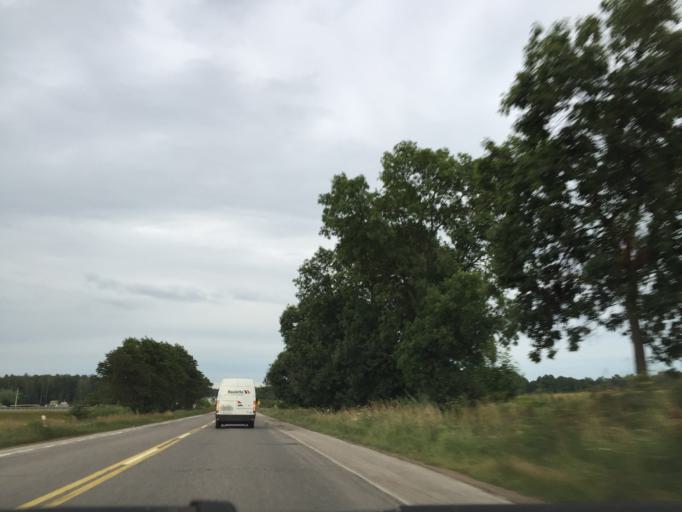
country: PL
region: Podlasie
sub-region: Powiat wysokomazowiecki
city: Sokoly
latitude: 53.1227
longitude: 22.6660
